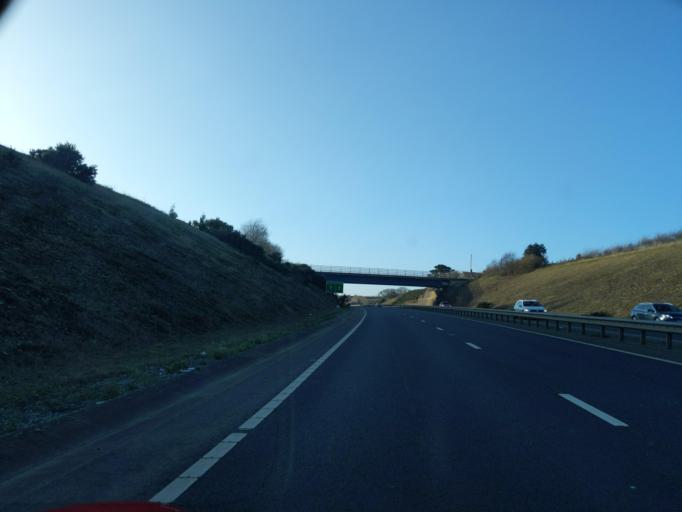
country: GB
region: England
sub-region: Cornwall
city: Liskeard
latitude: 50.4602
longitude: -4.5157
